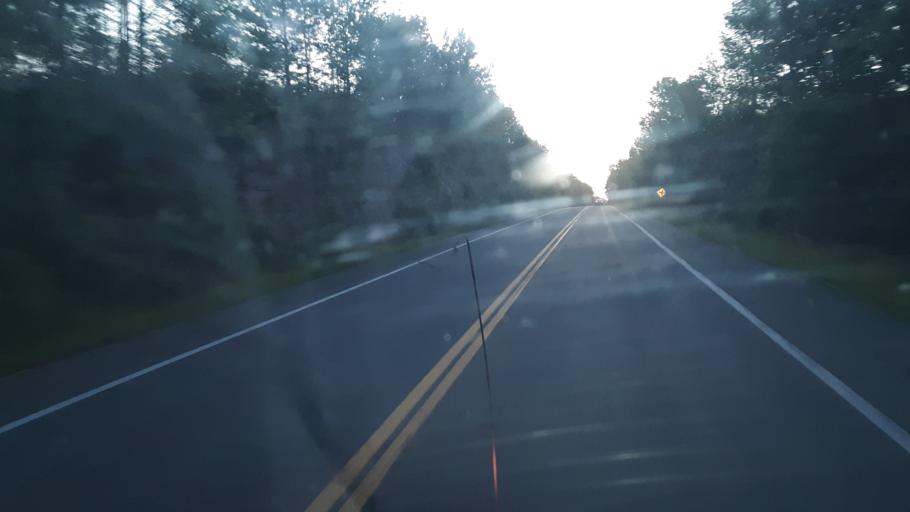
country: US
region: New York
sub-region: Montgomery County
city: Hagaman
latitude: 42.9721
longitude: -74.0735
